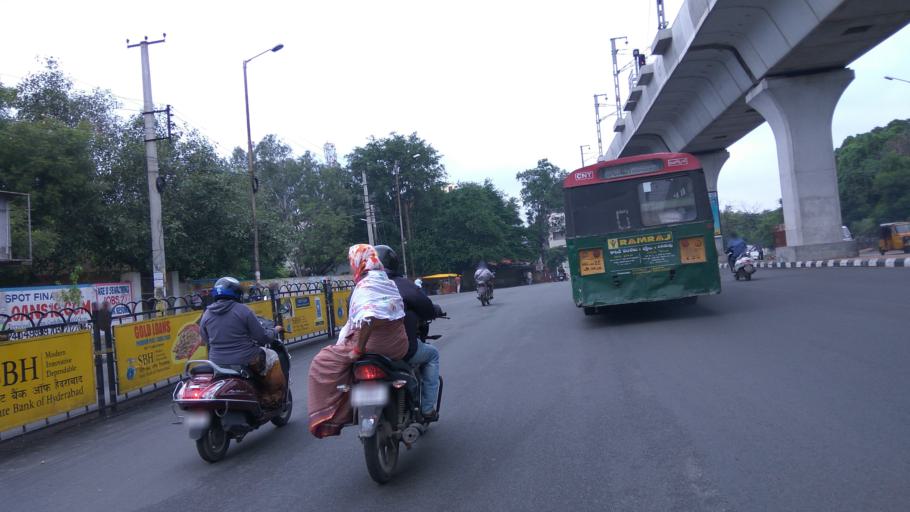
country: IN
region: Telangana
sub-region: Hyderabad
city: Malkajgiri
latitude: 17.4341
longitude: 78.5210
